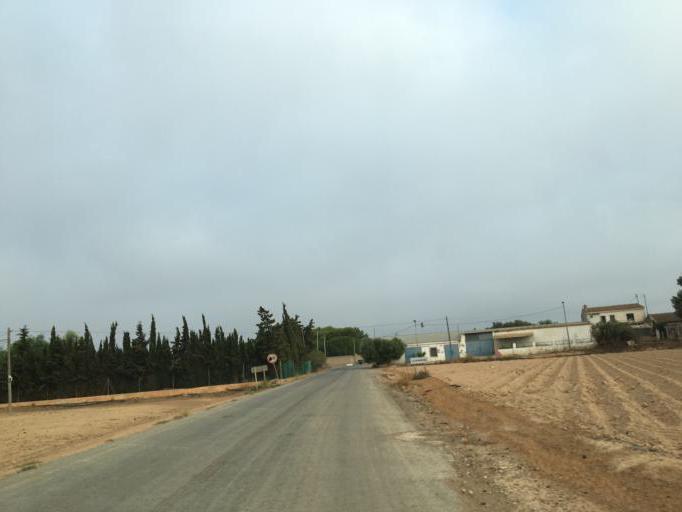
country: ES
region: Murcia
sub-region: Murcia
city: Cartagena
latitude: 37.6643
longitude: -0.9508
